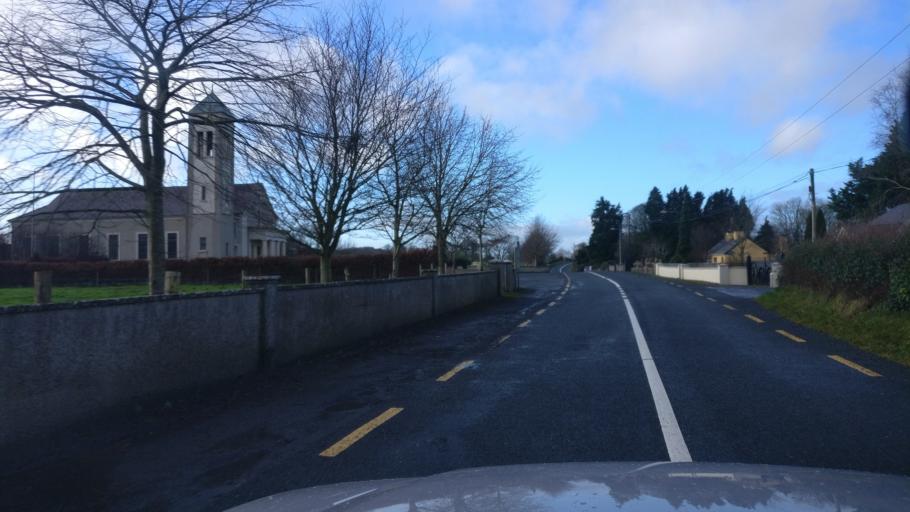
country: IE
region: Connaught
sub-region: County Galway
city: Athenry
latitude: 53.2517
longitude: -8.6698
